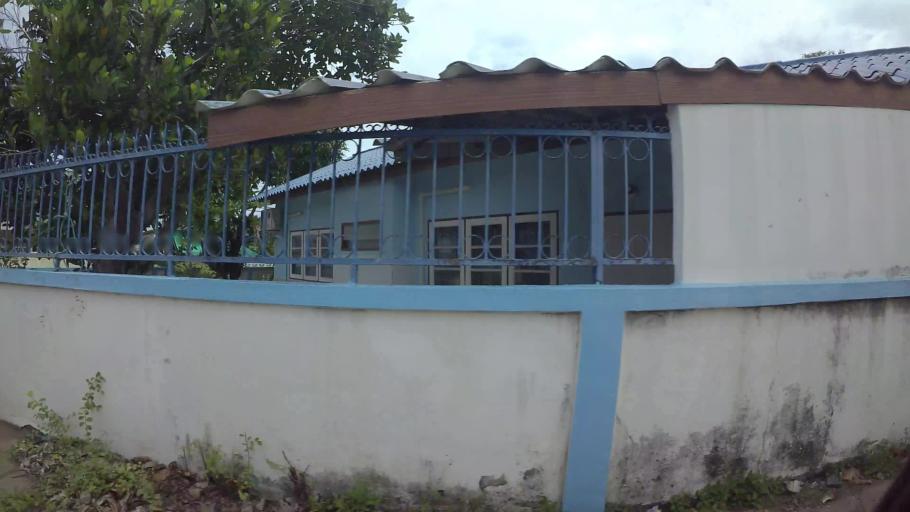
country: TH
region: Chon Buri
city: Sattahip
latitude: 12.6757
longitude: 100.9051
